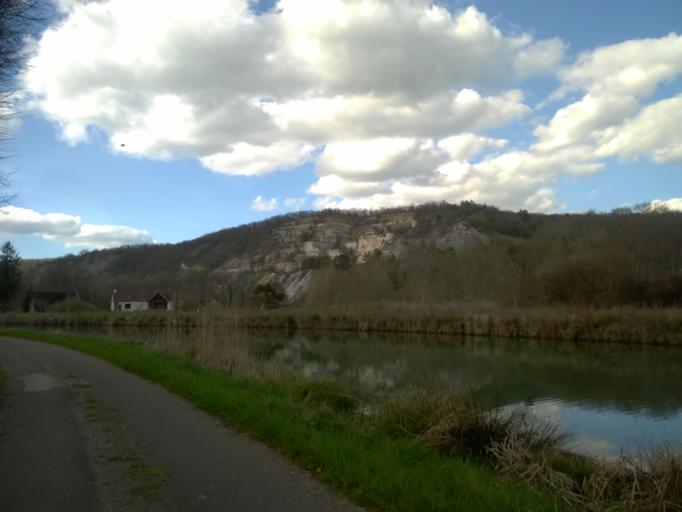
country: FR
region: Bourgogne
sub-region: Departement de l'Yonne
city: Ravieres
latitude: 47.7094
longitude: 4.2435
